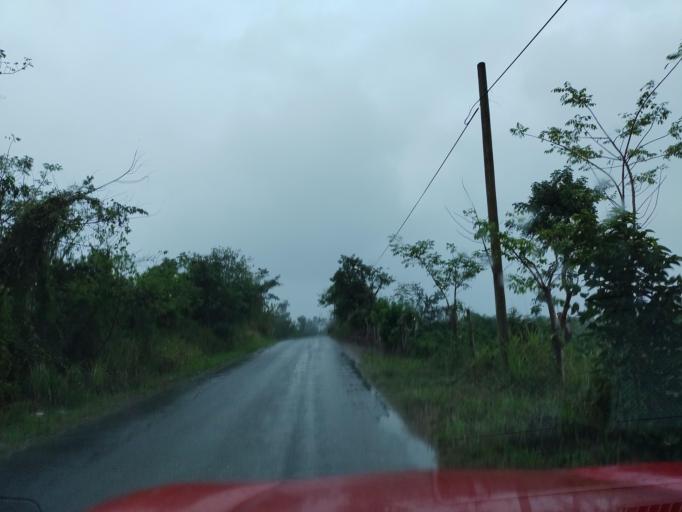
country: MX
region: Veracruz
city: Agua Dulce
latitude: 20.3366
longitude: -97.3127
